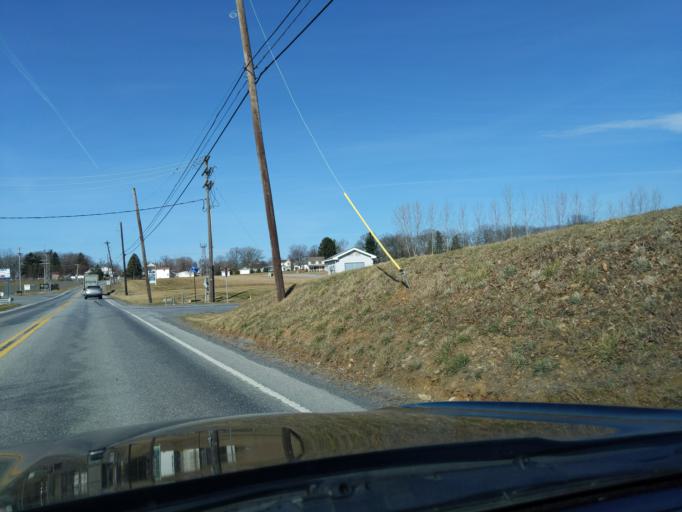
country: US
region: Pennsylvania
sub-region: Blair County
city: Martinsburg
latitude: 40.3091
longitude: -78.3126
